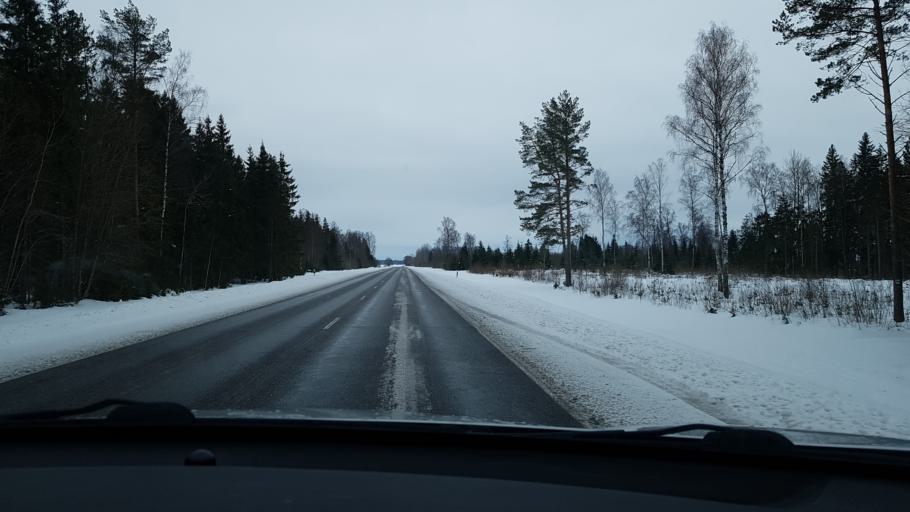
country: EE
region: Jaervamaa
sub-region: Jaerva-Jaani vald
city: Jarva-Jaani
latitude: 59.1313
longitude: 25.7784
